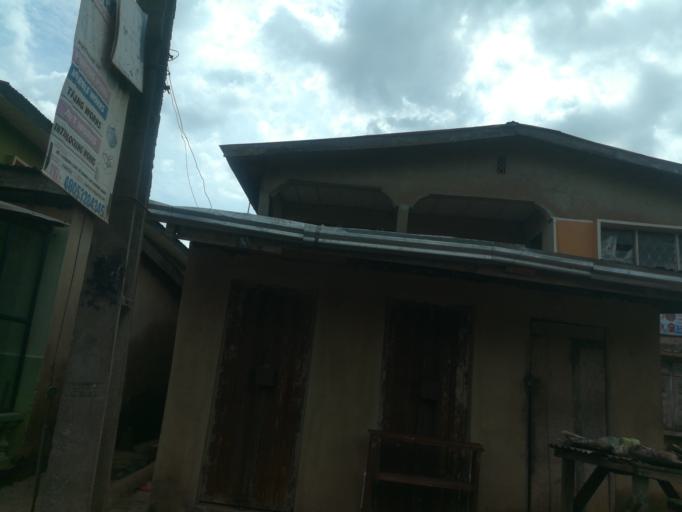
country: NG
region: Oyo
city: Ibadan
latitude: 7.4173
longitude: 3.9327
